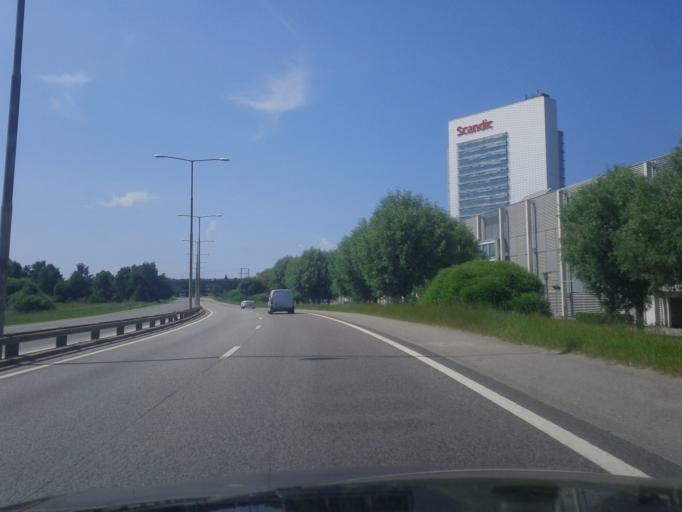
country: SE
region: Stockholm
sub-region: Stockholms Kommun
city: Arsta
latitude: 59.2777
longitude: 18.0198
